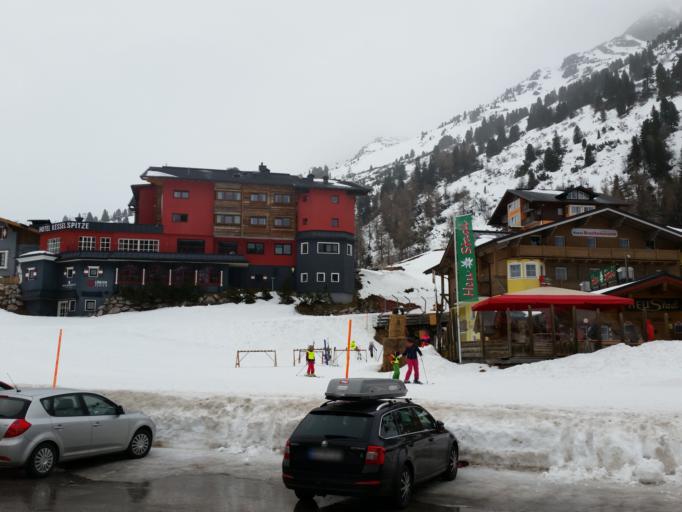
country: AT
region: Salzburg
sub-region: Politischer Bezirk Tamsweg
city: Tweng
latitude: 47.2410
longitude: 13.5713
